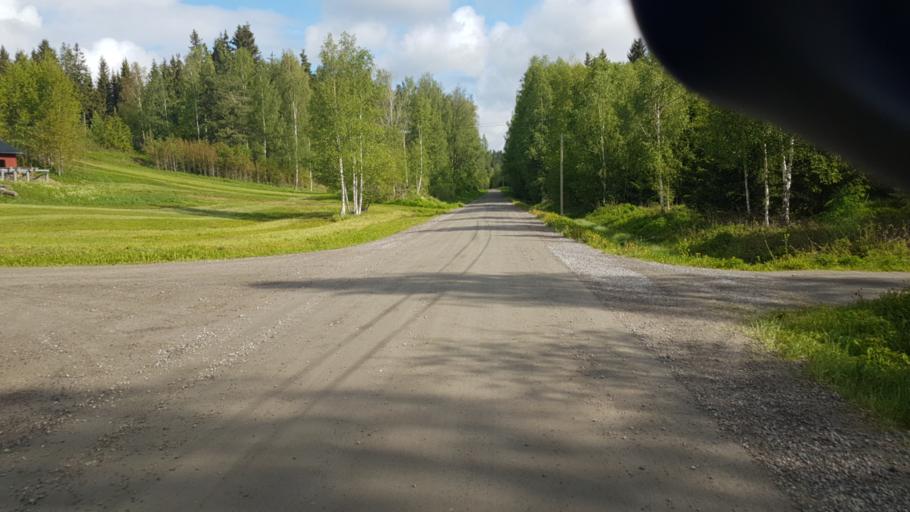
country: NO
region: Hedmark
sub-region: Eidskog
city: Skotterud
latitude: 59.8503
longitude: 11.9850
